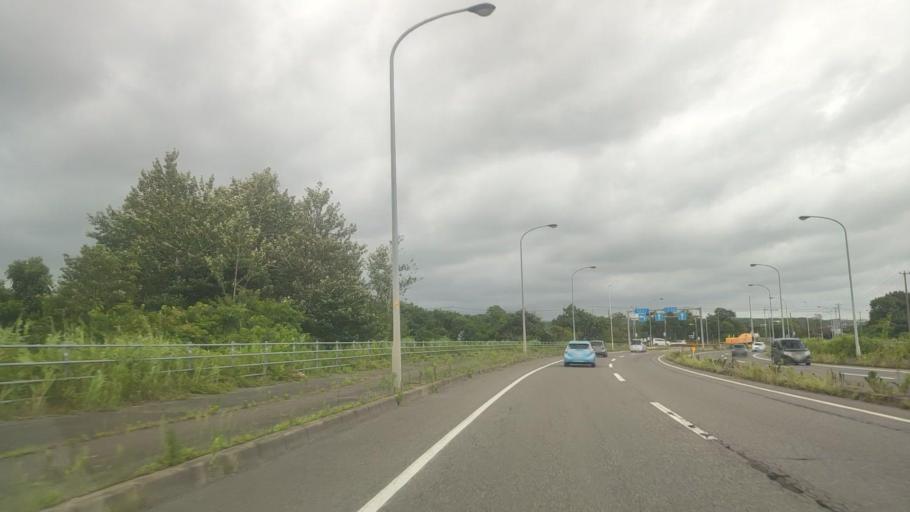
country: JP
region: Hokkaido
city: Shiraoi
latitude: 42.5623
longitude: 141.3810
